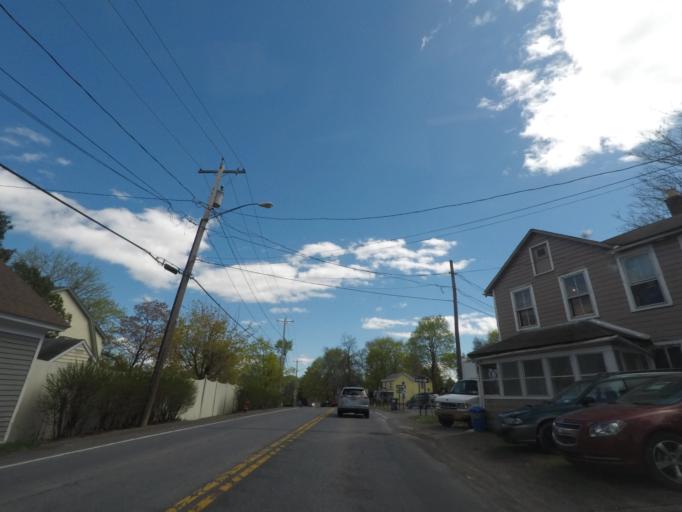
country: US
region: New York
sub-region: Columbia County
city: Oakdale
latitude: 42.2457
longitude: -73.7711
